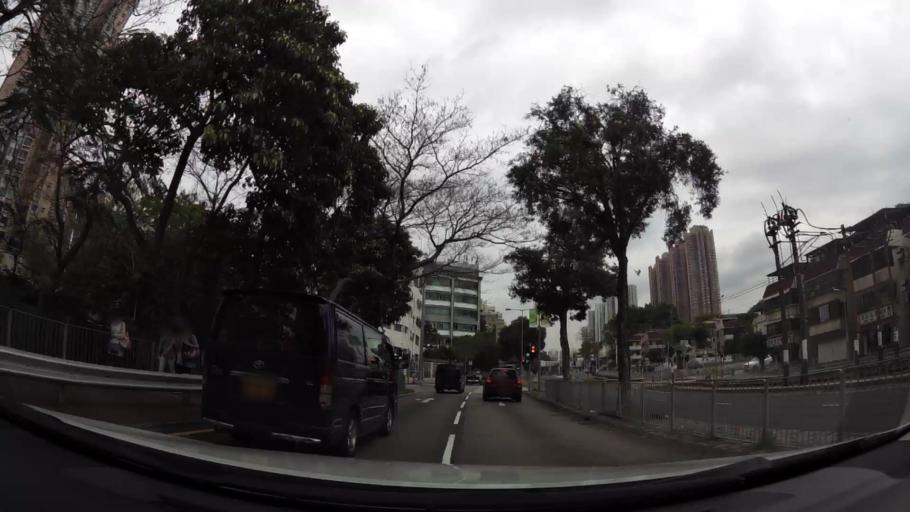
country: HK
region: Tuen Mun
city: Tuen Mun
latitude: 22.3990
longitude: 113.9773
